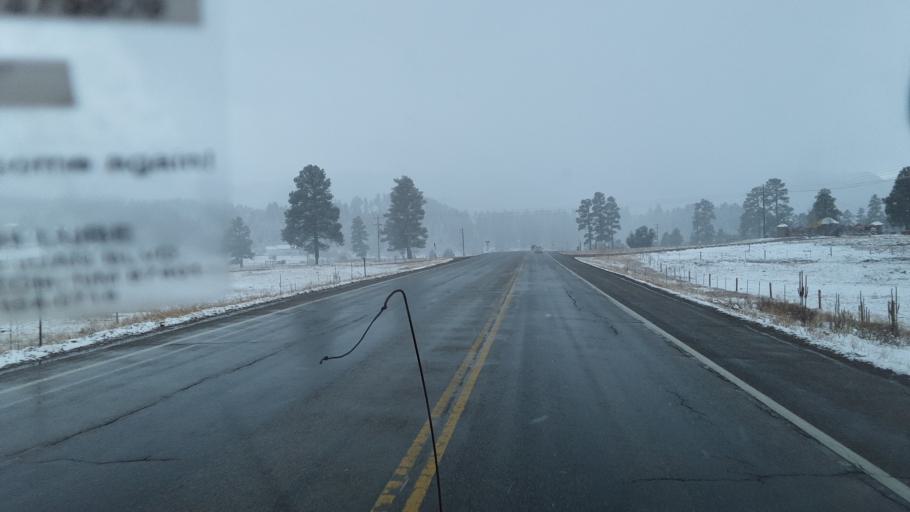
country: US
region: Colorado
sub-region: Archuleta County
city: Pagosa Springs
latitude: 37.2331
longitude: -107.1056
